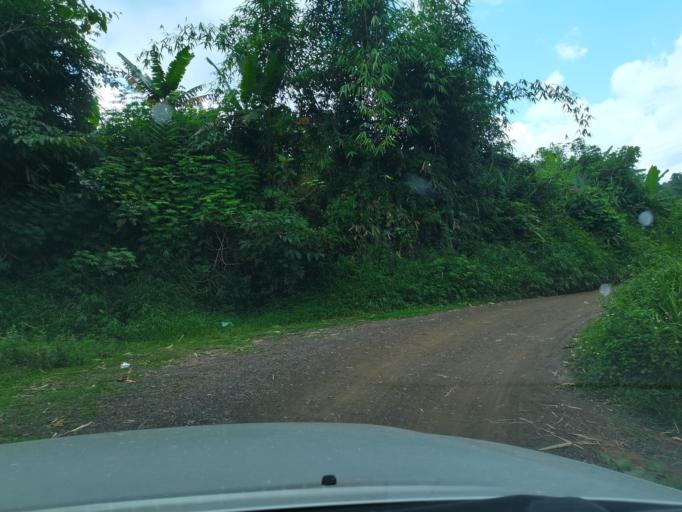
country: LA
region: Loungnamtha
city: Muang Long
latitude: 20.7576
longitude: 101.0170
